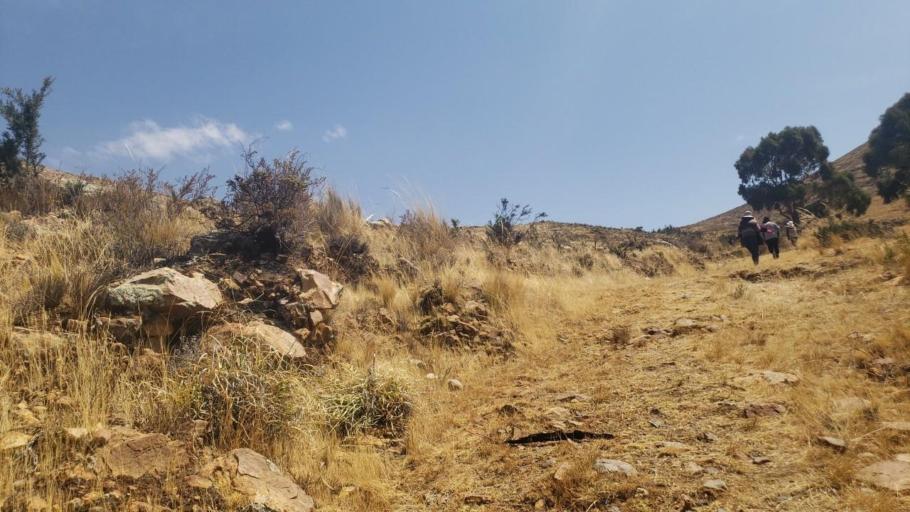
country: BO
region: La Paz
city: Batallas
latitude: -16.3494
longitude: -68.6479
